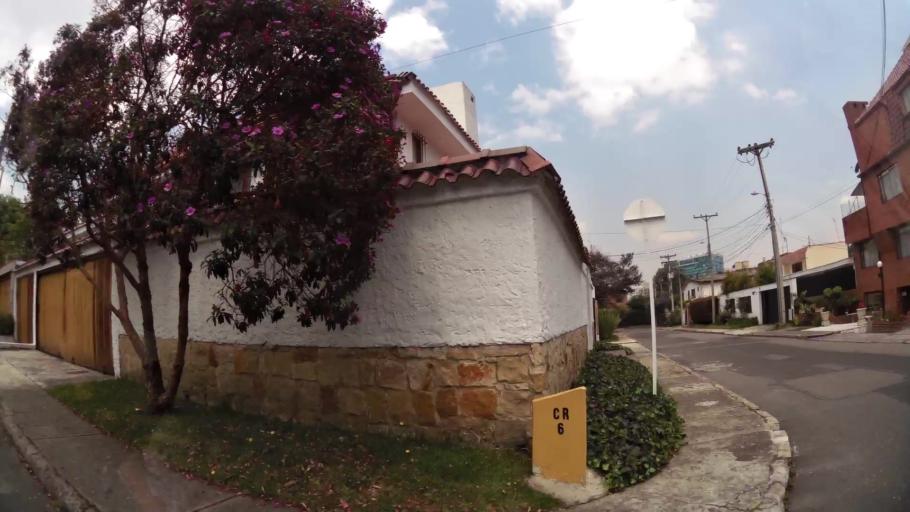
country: CO
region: Bogota D.C.
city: Barrio San Luis
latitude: 4.6881
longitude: -74.0338
